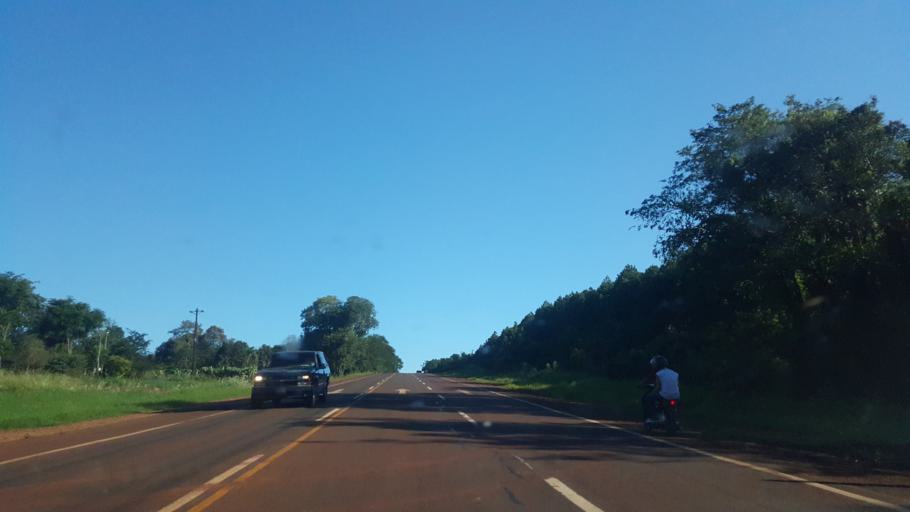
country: AR
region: Misiones
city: Puerto Esperanza
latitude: -26.1566
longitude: -54.5832
